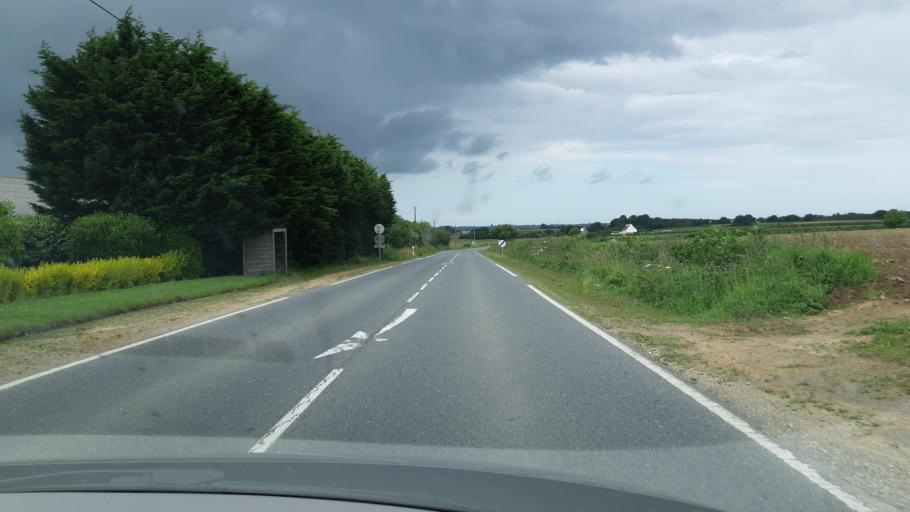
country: FR
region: Brittany
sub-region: Departement du Finistere
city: Plouvorn
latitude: 48.5934
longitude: -4.0511
